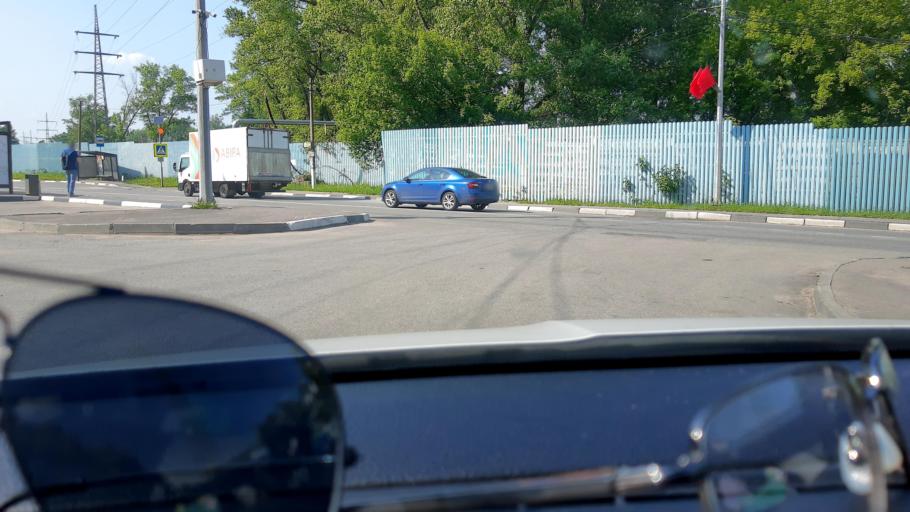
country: RU
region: Moskovskaya
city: Lobnya
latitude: 56.0192
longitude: 37.4303
